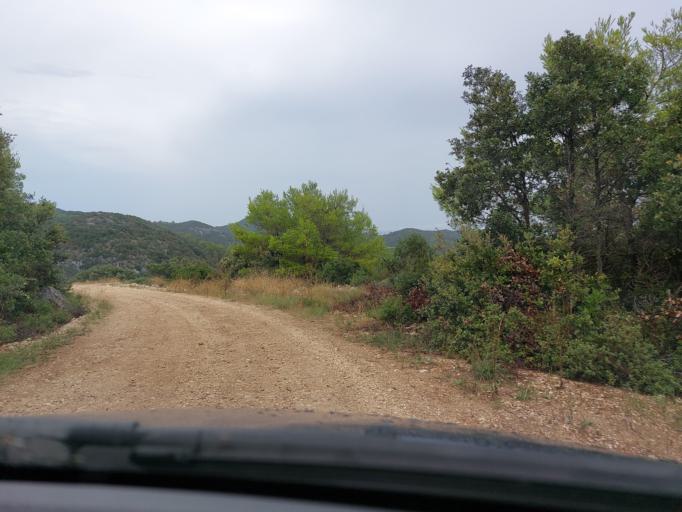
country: HR
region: Dubrovacko-Neretvanska
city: Smokvica
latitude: 42.7475
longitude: 16.9168
